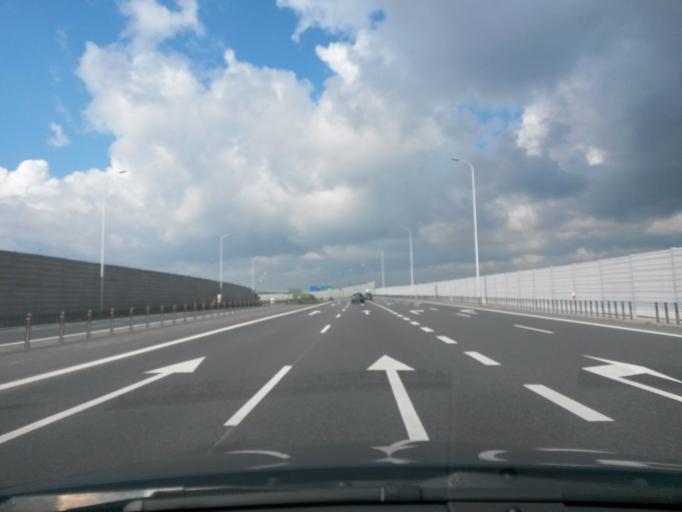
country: PL
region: Masovian Voivodeship
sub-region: Powiat pruszkowski
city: Piastow
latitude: 52.1963
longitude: 20.8528
